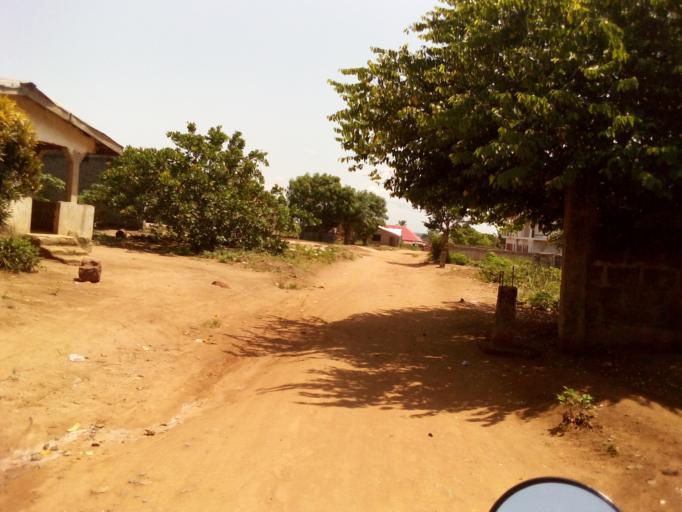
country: SL
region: Western Area
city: Waterloo
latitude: 8.3373
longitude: -13.0296
